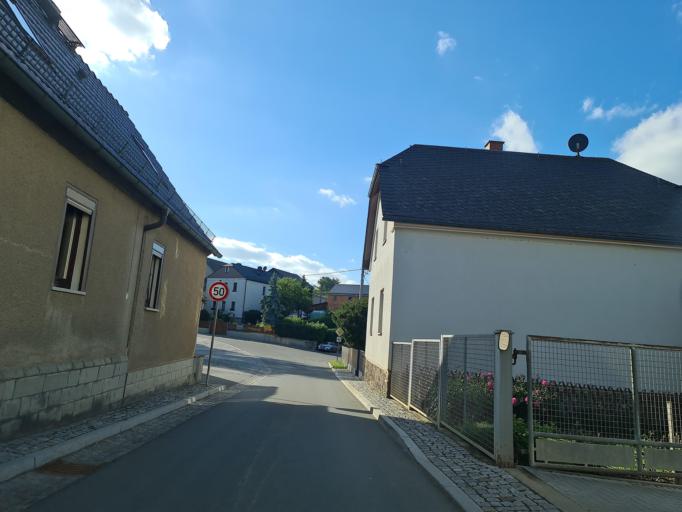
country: DE
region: Saxony
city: Mehltheuer
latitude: 50.4947
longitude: 12.0355
